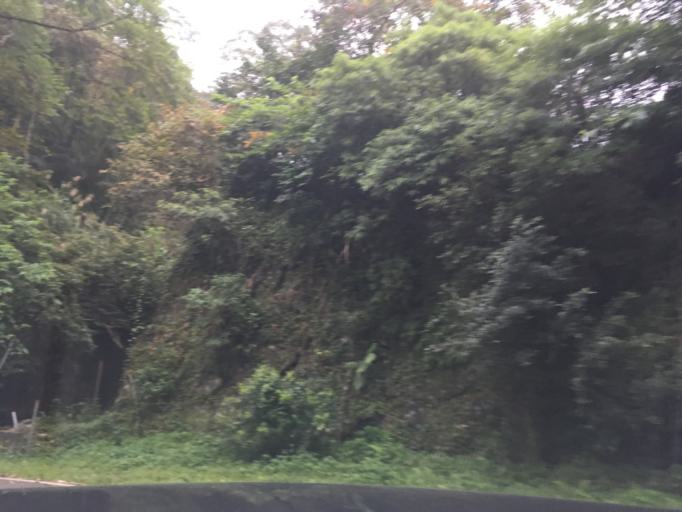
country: TW
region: Taiwan
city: Daxi
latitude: 24.8938
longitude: 121.3802
